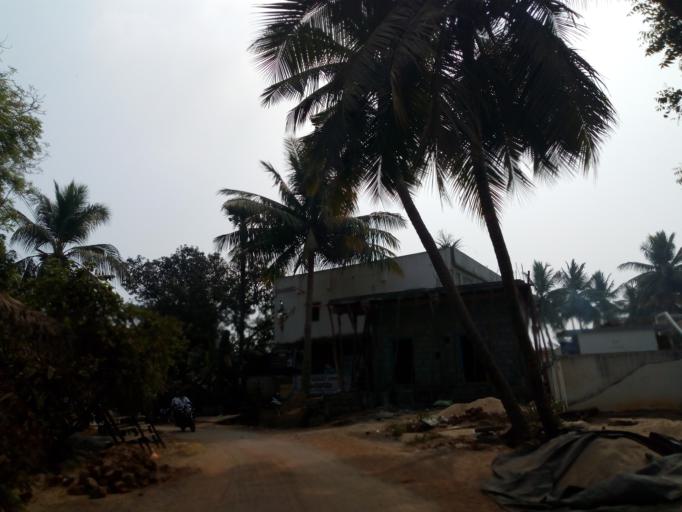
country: IN
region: Andhra Pradesh
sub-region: West Godavari
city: Tadepallegudem
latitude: 16.8734
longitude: 81.3186
